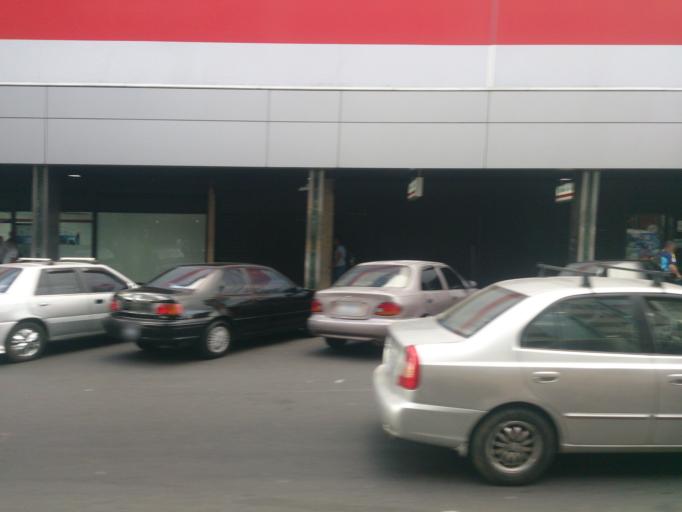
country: CR
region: San Jose
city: San Jose
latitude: 9.9336
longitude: -84.0812
